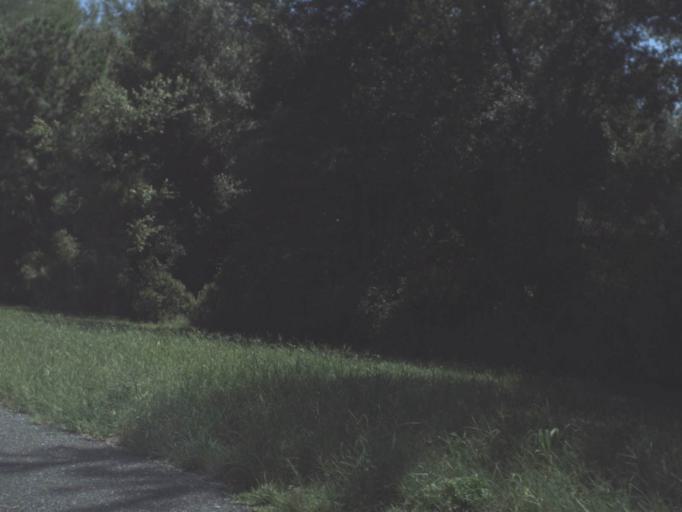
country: US
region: Florida
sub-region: Levy County
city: Inglis
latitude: 29.1556
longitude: -82.6385
